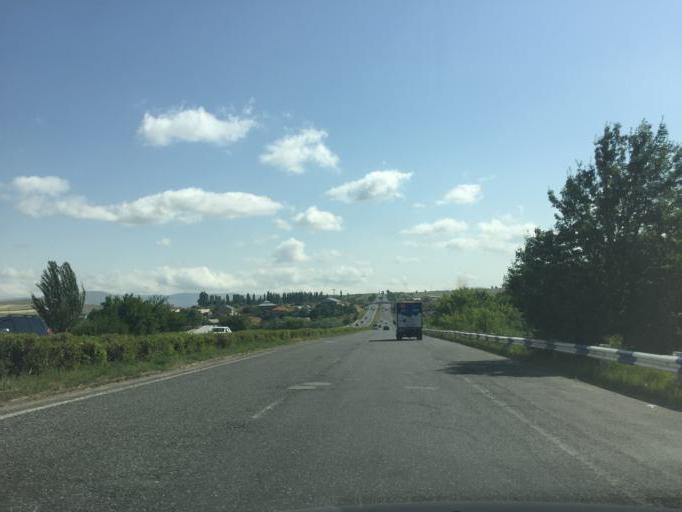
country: AM
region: Kotayk'i Marz
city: Hrazdan
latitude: 40.4877
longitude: 44.7711
